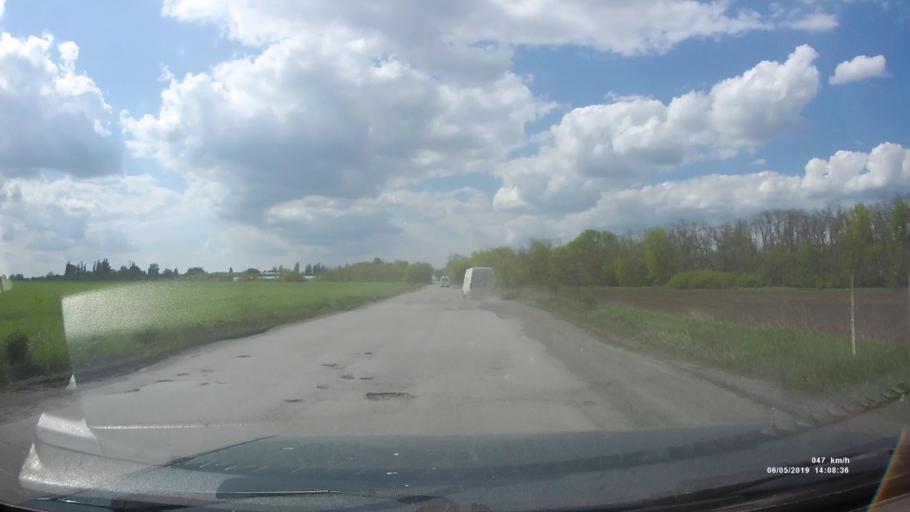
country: RU
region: Rostov
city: Shakhty
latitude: 47.6838
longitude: 40.2969
